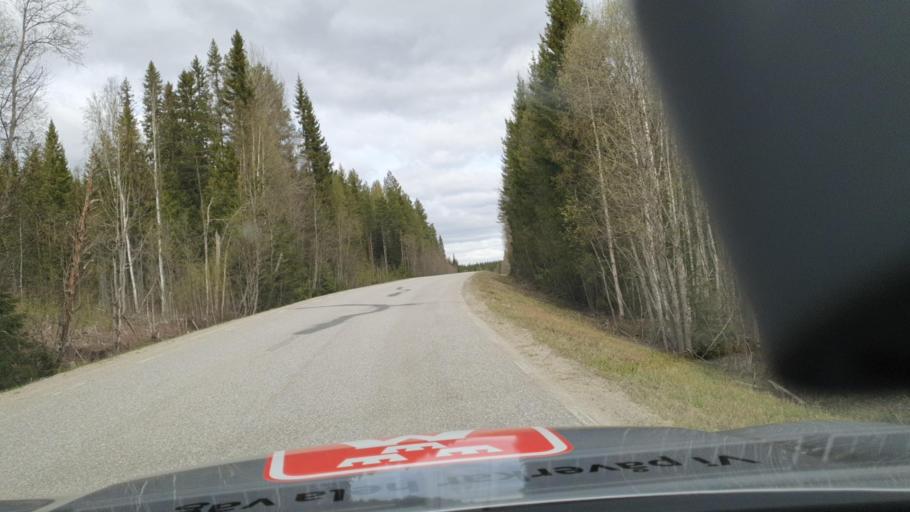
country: SE
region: Vaesternorrland
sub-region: OErnskoeldsviks Kommun
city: Ornskoldsvik
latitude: 63.6596
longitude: 18.7692
